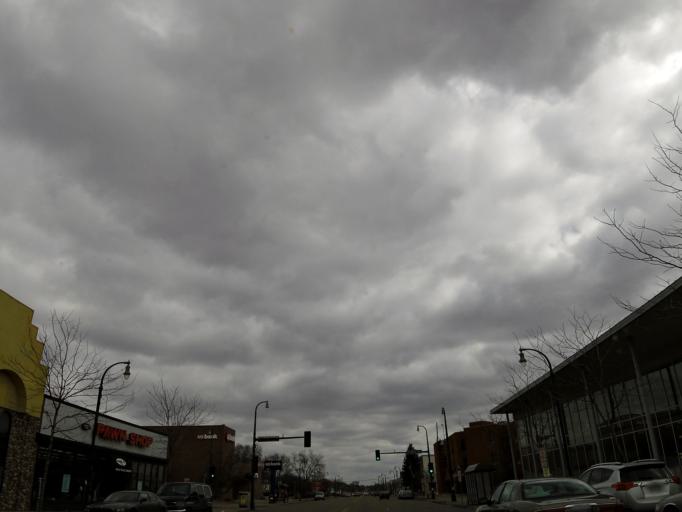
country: US
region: Minnesota
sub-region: Hennepin County
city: Minneapolis
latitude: 44.9484
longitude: -93.2323
